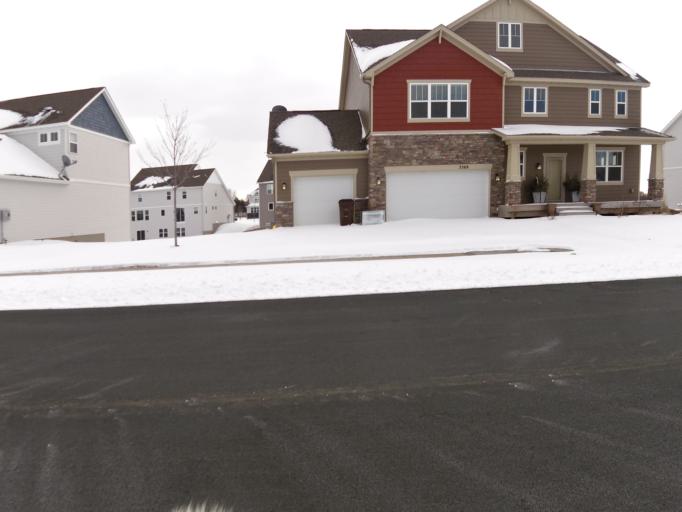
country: US
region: Minnesota
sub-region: Scott County
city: Prior Lake
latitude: 44.6908
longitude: -93.4541
